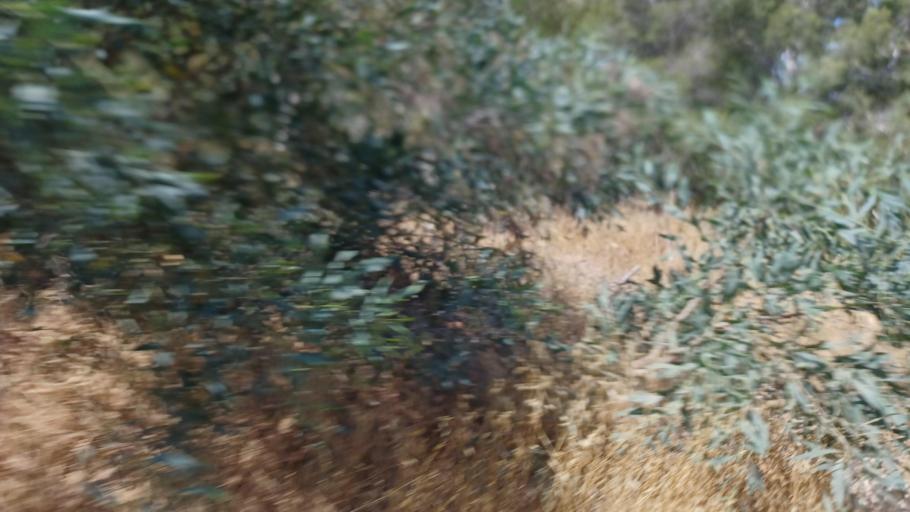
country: CY
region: Ammochostos
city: Paralimni
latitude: 35.0048
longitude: 33.9577
